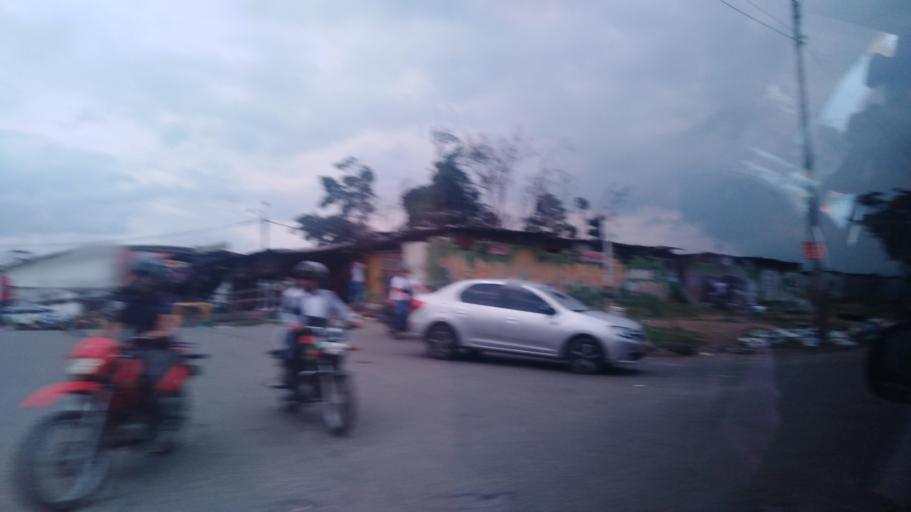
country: CO
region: Valle del Cauca
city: Cali
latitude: 3.4254
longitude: -76.5203
